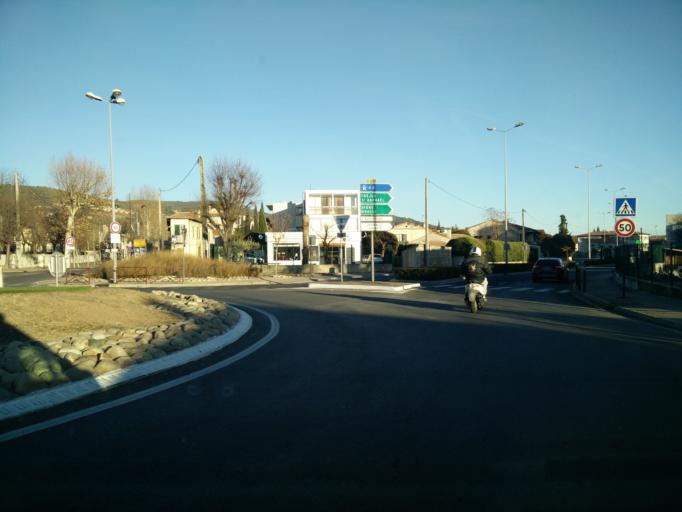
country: FR
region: Provence-Alpes-Cote d'Azur
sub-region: Departement du Var
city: Draguignan
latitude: 43.5346
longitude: 6.4559
